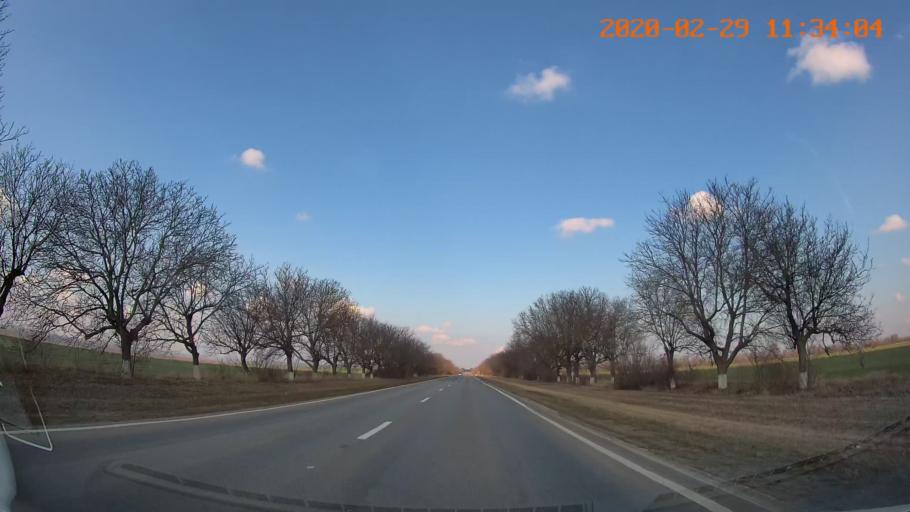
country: MD
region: Rezina
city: Saharna
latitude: 47.5602
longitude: 29.0779
